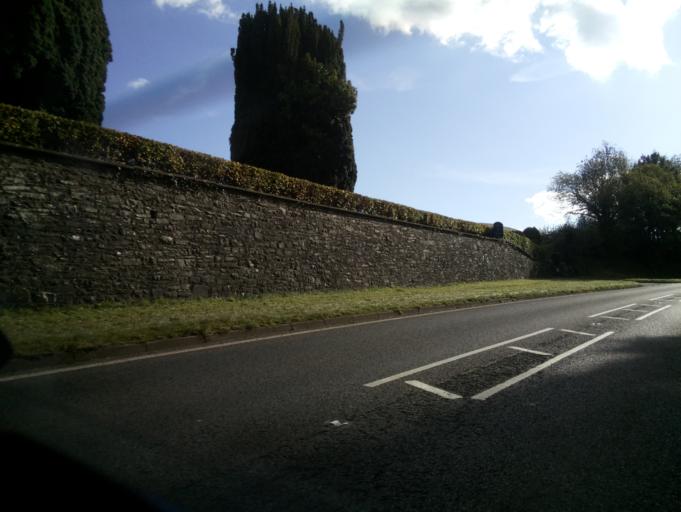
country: GB
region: Wales
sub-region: Sir Powys
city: Brecon
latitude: 51.9192
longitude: -3.4649
